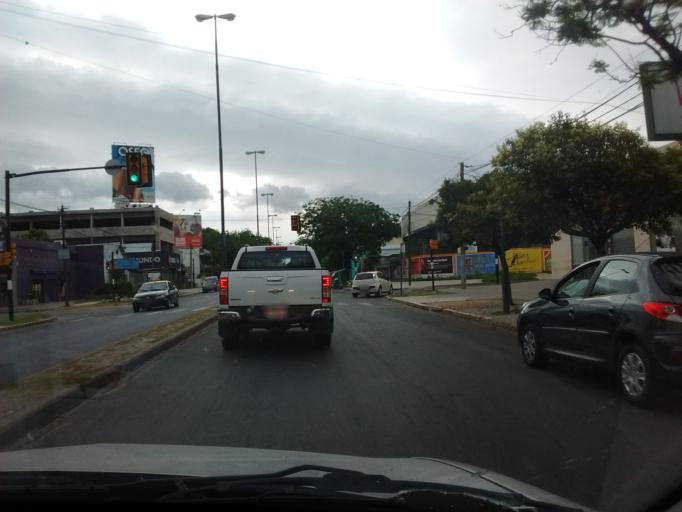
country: AR
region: Santa Fe
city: Granadero Baigorria
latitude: -32.9295
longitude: -60.7328
